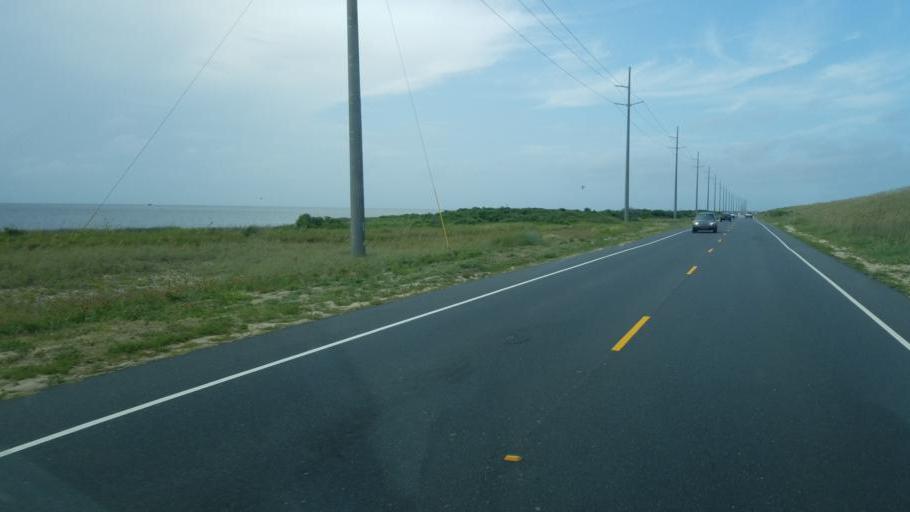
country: US
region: North Carolina
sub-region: Dare County
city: Buxton
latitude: 35.2803
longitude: -75.5171
